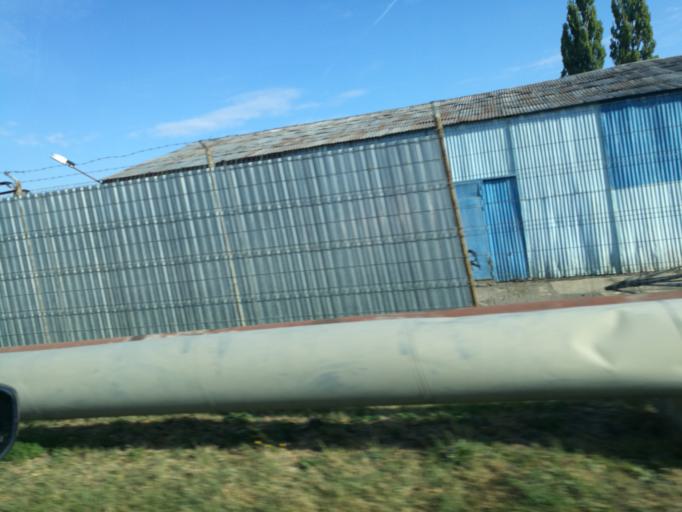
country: RO
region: Bihor
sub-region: Comuna Biharea
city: Oradea
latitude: 47.0394
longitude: 21.9340
